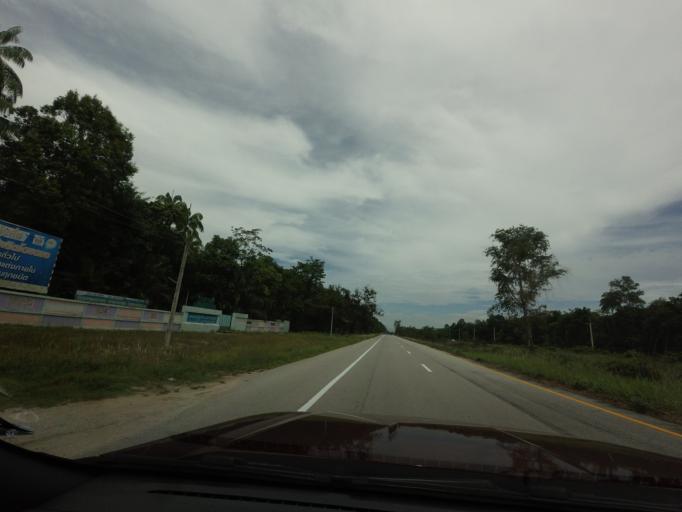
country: TH
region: Narathiwat
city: Narathiwat
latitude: 6.3499
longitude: 101.8887
